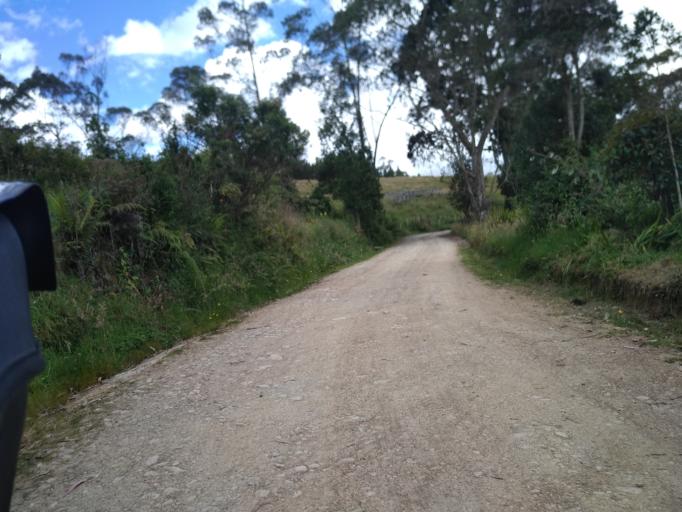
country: CO
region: Boyaca
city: Duitama
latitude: 5.9404
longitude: -73.1243
